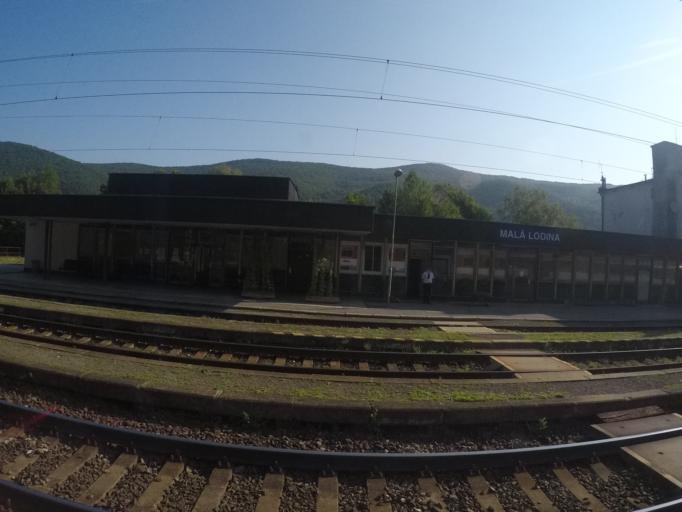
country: SK
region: Presovsky
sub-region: Okres Presov
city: Presov
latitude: 48.8740
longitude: 21.1341
